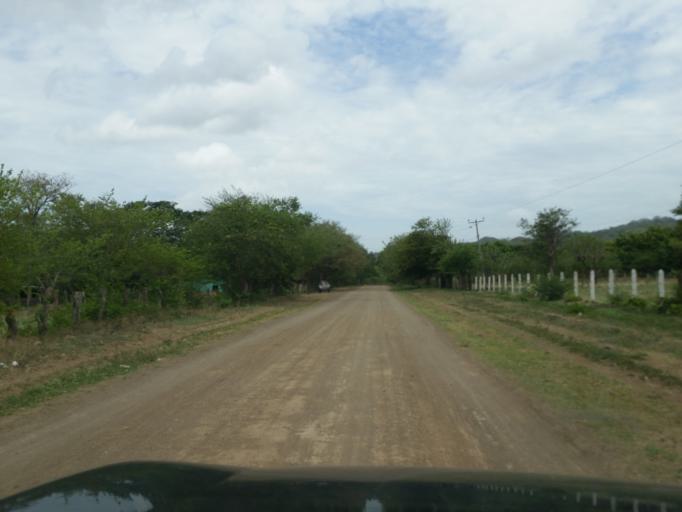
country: NI
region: Granada
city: Nandaime
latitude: 11.6497
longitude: -85.9891
